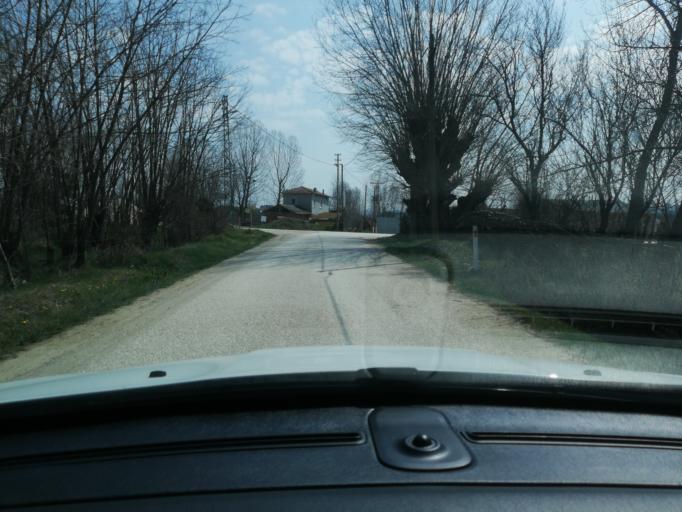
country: TR
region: Kastamonu
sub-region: Cide
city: Kastamonu
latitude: 41.4574
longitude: 33.7670
